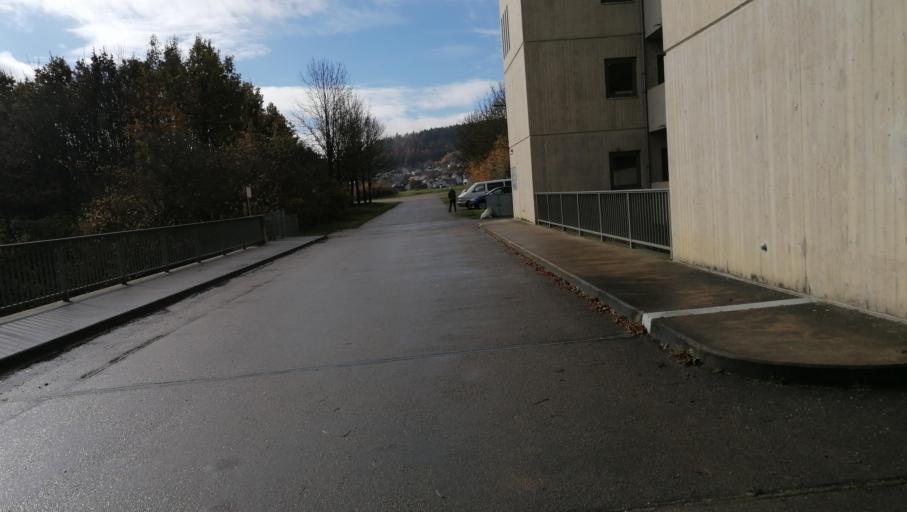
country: DE
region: Bavaria
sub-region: Upper Palatinate
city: Dietfurt
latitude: 49.0327
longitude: 11.5618
